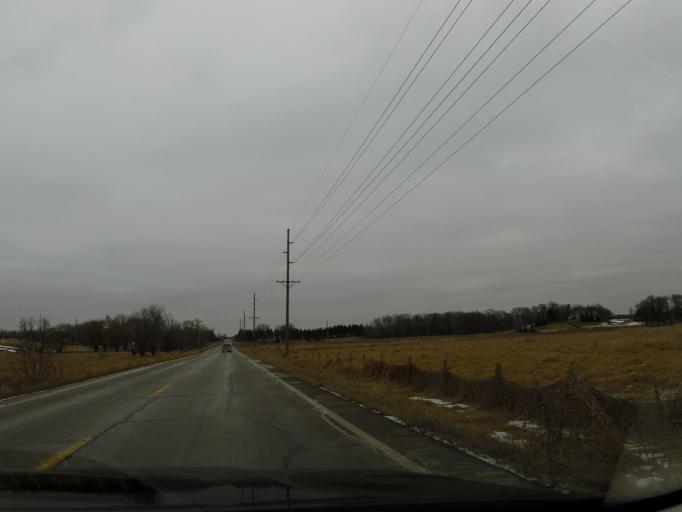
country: US
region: Minnesota
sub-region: Hennepin County
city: Independence
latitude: 45.0179
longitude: -93.7272
